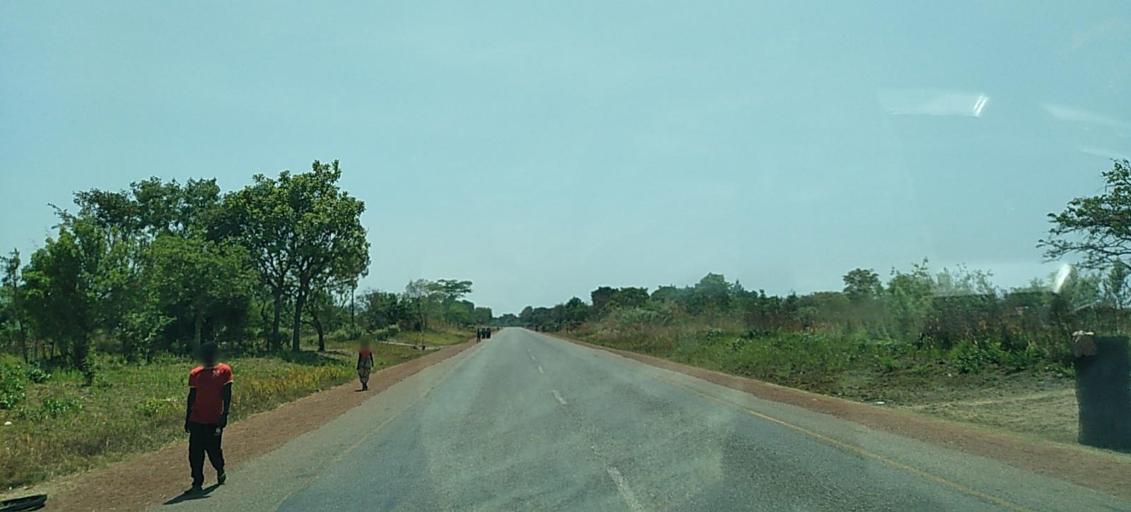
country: ZM
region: North-Western
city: Solwezi
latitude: -12.4041
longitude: 26.1418
